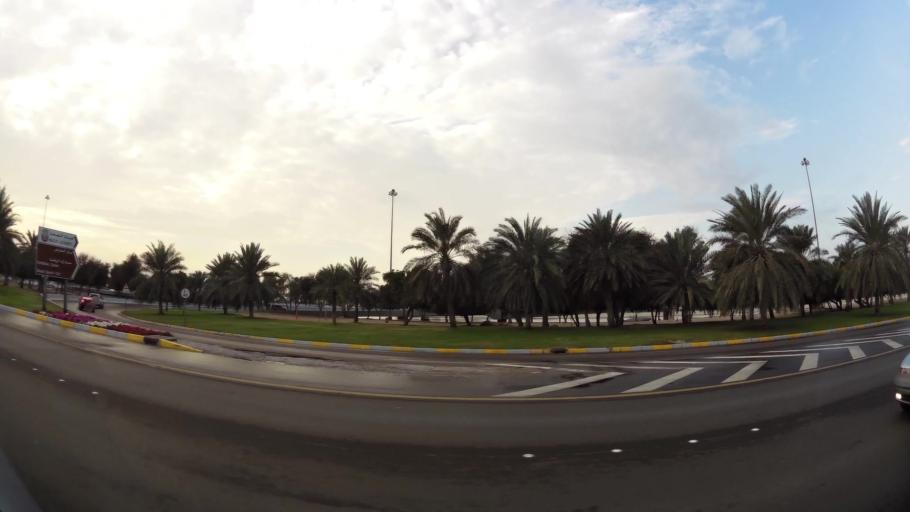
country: AE
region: Abu Dhabi
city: Abu Dhabi
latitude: 24.4148
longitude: 54.4448
